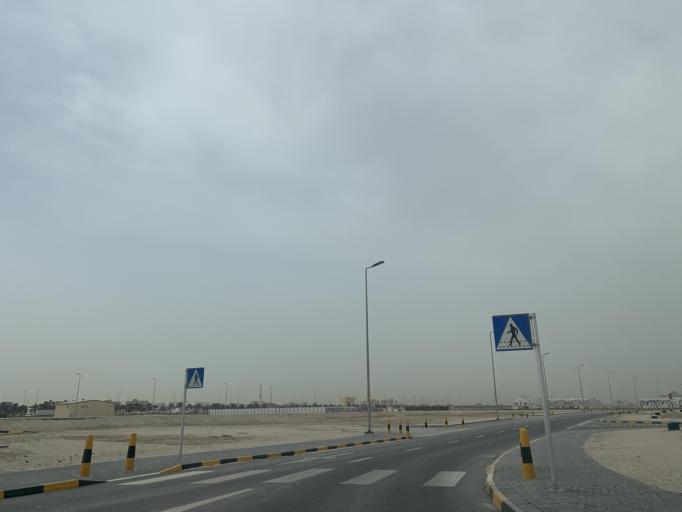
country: BH
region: Northern
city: Madinat `Isa
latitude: 26.1846
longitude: 50.5084
